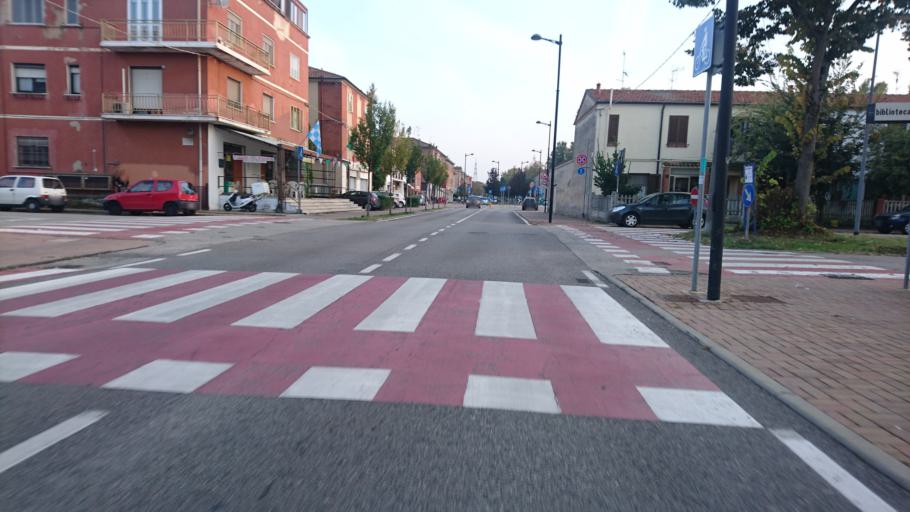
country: IT
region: Emilia-Romagna
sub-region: Provincia di Ferrara
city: Ferrara
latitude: 44.8638
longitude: 11.6066
